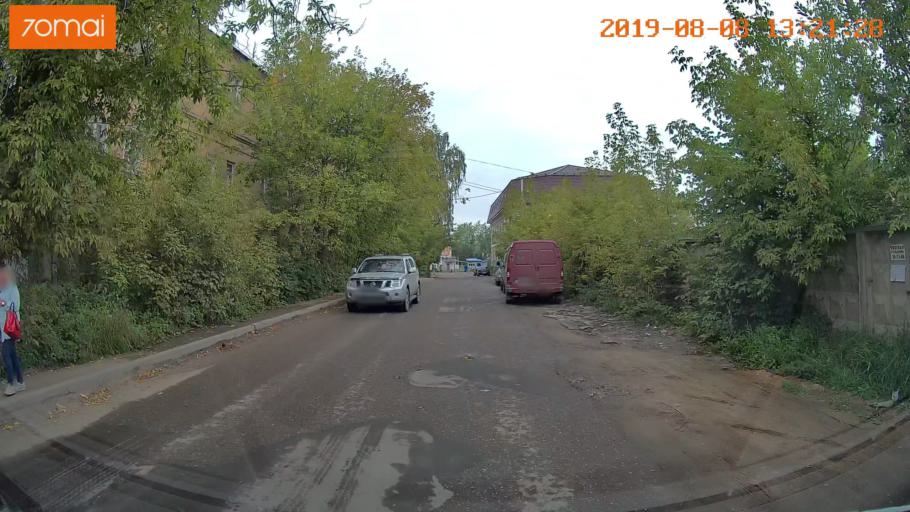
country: RU
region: Ivanovo
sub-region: Gorod Ivanovo
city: Ivanovo
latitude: 57.0105
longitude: 40.9529
